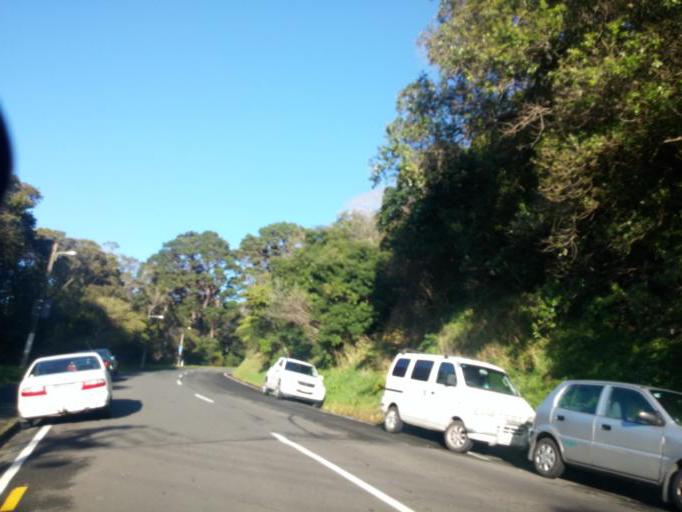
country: NZ
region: Wellington
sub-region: Wellington City
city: Wellington
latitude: -41.2977
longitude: 174.7681
